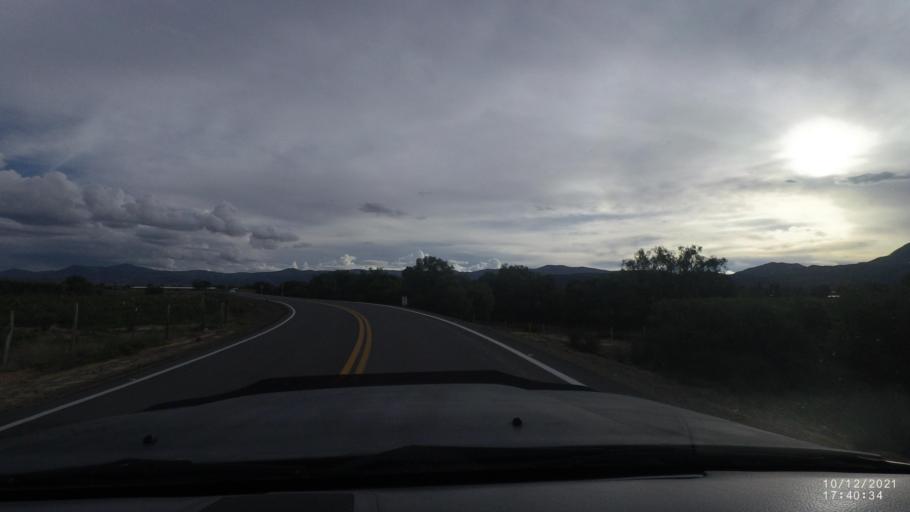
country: BO
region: Cochabamba
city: Tarata
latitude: -17.5874
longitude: -66.0195
